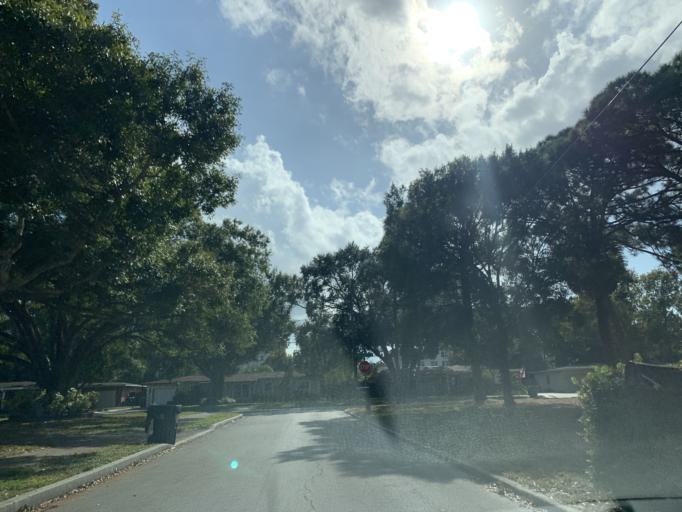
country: US
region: Florida
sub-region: Hillsborough County
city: Tampa
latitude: 27.9011
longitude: -82.5170
